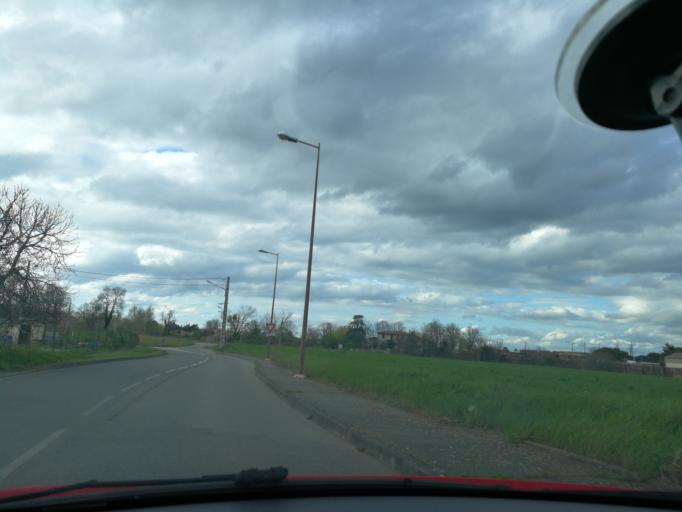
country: FR
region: Midi-Pyrenees
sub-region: Departement de la Haute-Garonne
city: Blagnac
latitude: 43.6376
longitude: 1.4115
